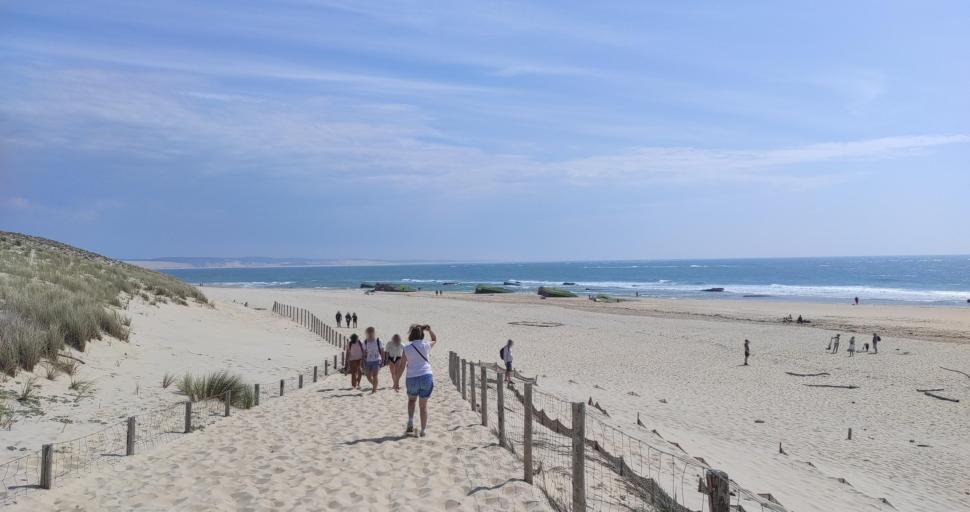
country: FR
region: Aquitaine
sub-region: Departement de la Gironde
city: Arcachon
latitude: 44.6266
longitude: -1.2572
